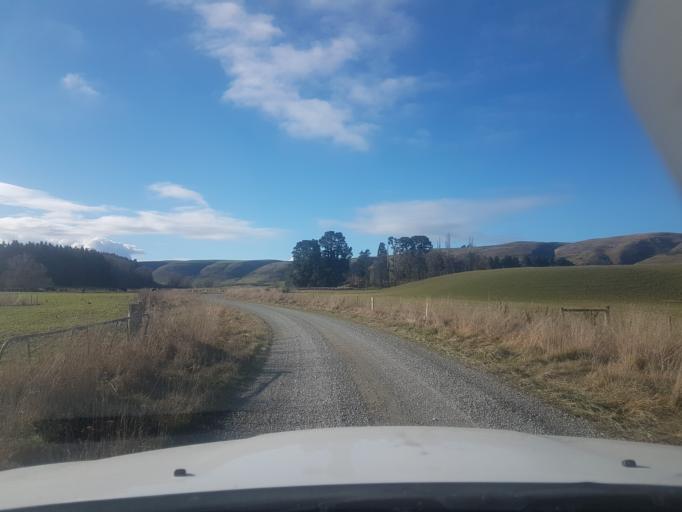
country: NZ
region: Canterbury
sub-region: Timaru District
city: Pleasant Point
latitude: -44.1764
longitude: 170.8612
